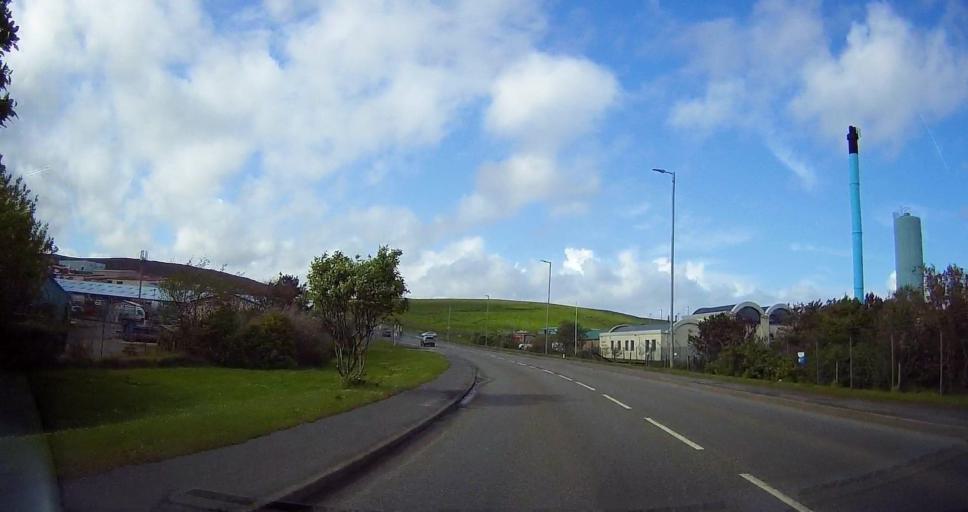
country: GB
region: Scotland
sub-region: Shetland Islands
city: Lerwick
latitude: 60.1669
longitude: -1.1651
